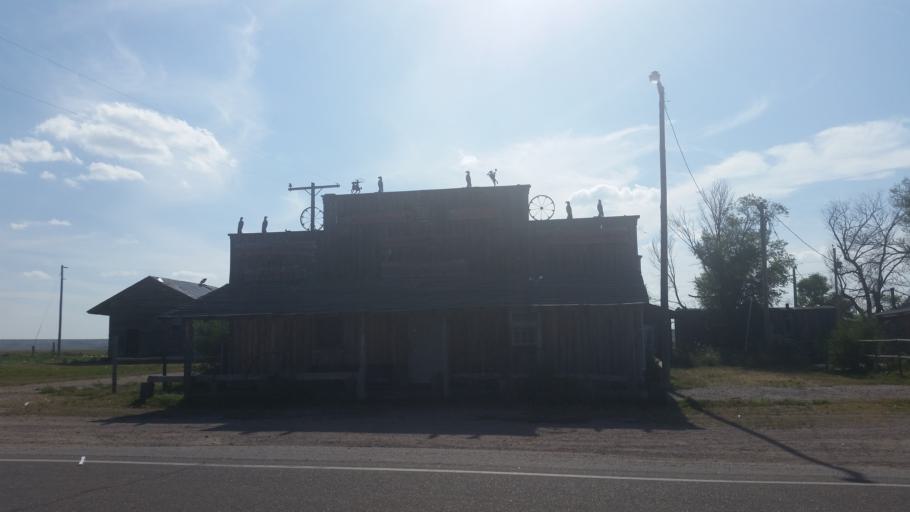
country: US
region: South Dakota
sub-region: Shannon County
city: Porcupine
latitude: 43.7798
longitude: -102.5546
